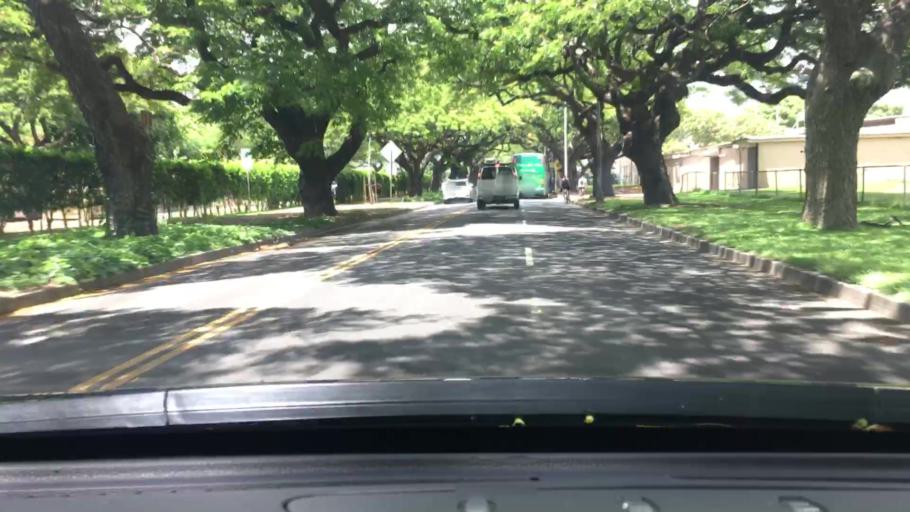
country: US
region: Hawaii
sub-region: Honolulu County
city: Honolulu
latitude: 21.2713
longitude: -157.8162
